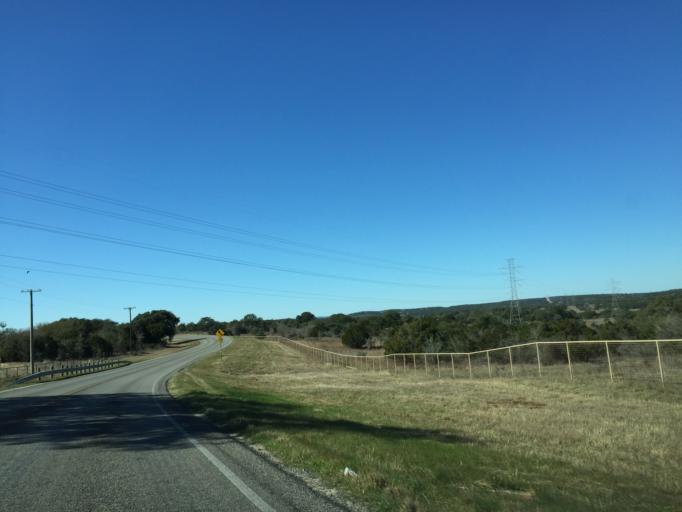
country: US
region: Texas
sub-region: Comal County
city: Canyon Lake
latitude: 29.7650
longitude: -98.3013
